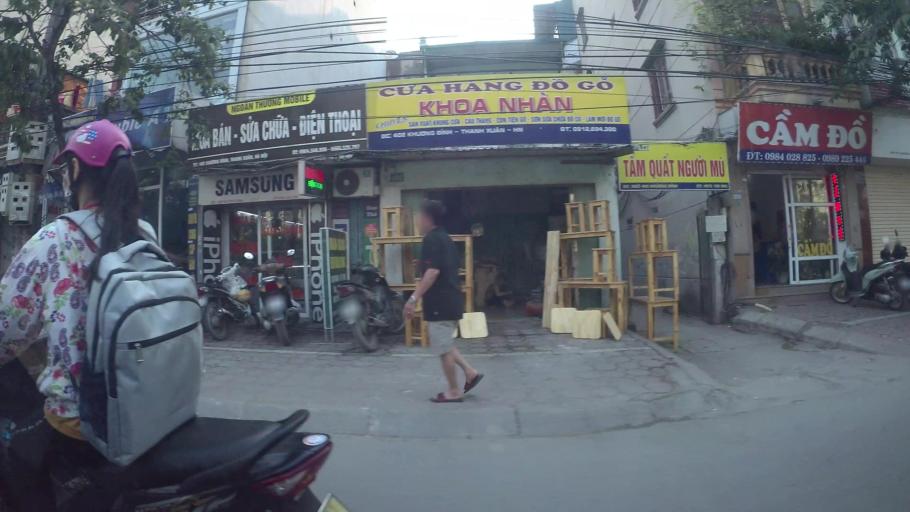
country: VN
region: Ha Noi
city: Thanh Xuan
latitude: 20.9880
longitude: 105.8129
